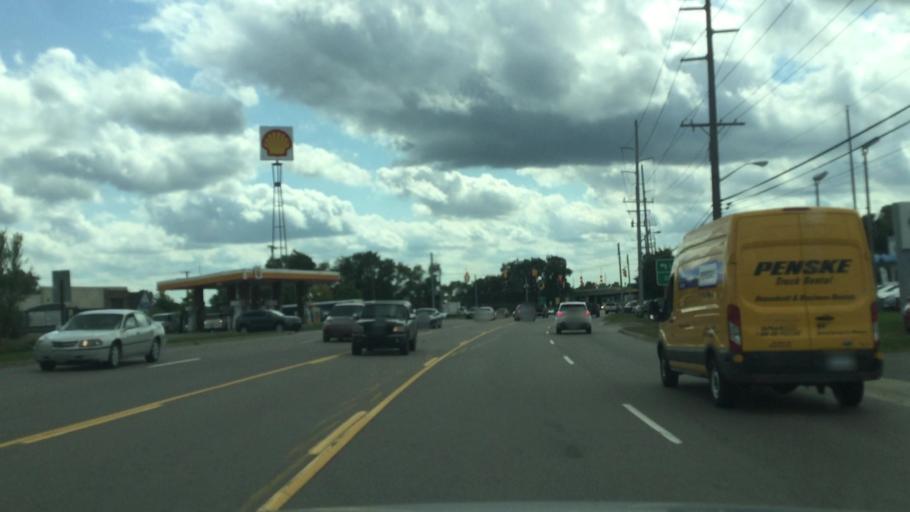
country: US
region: Michigan
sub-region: Livingston County
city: Brighton
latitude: 42.5511
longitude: -83.7896
